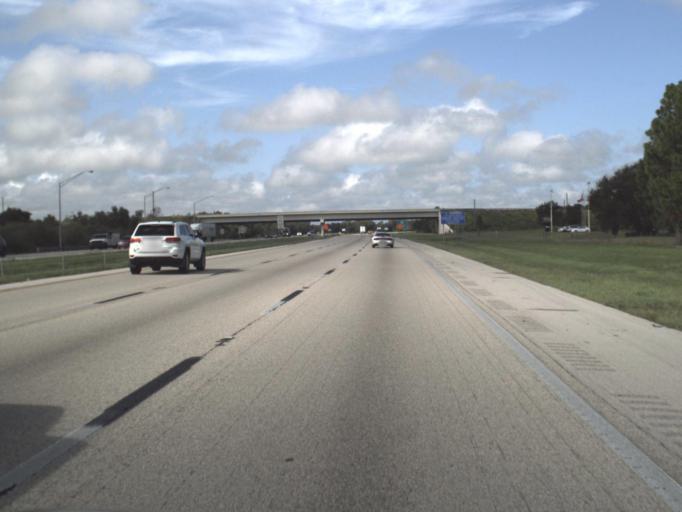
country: US
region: Florida
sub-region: Polk County
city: Polk City
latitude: 28.1676
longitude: -81.7743
